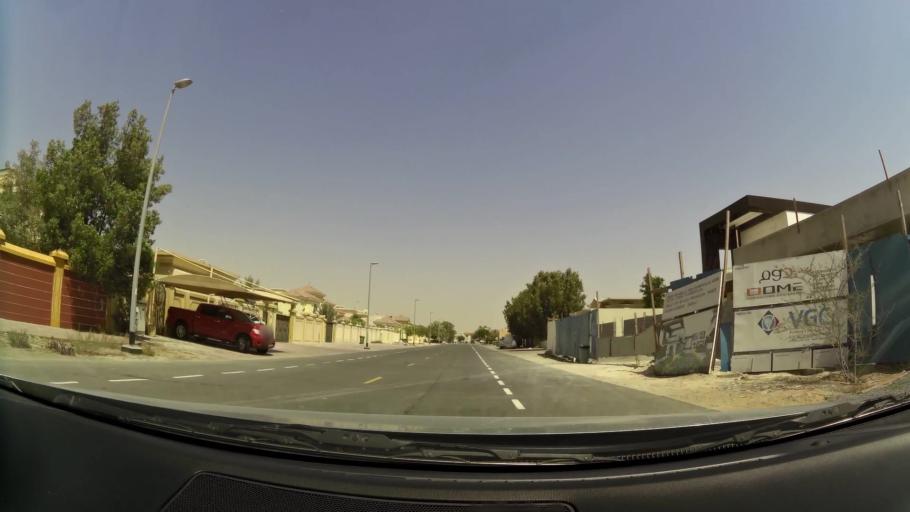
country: AE
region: Dubai
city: Dubai
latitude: 25.1050
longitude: 55.2101
